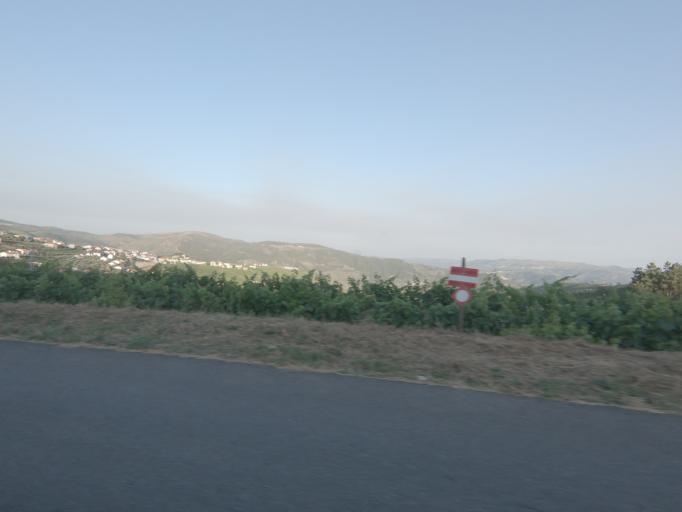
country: PT
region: Vila Real
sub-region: Sabrosa
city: Vilela
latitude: 41.2083
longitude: -7.6740
